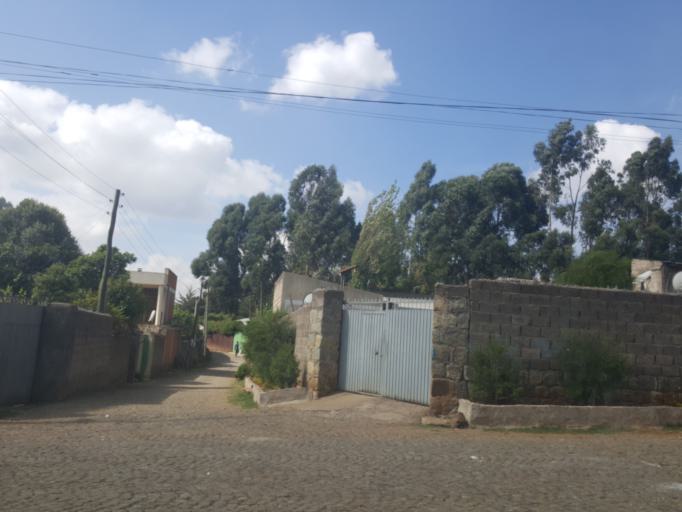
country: ET
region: Adis Abeba
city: Addis Ababa
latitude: 9.0534
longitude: 38.7261
